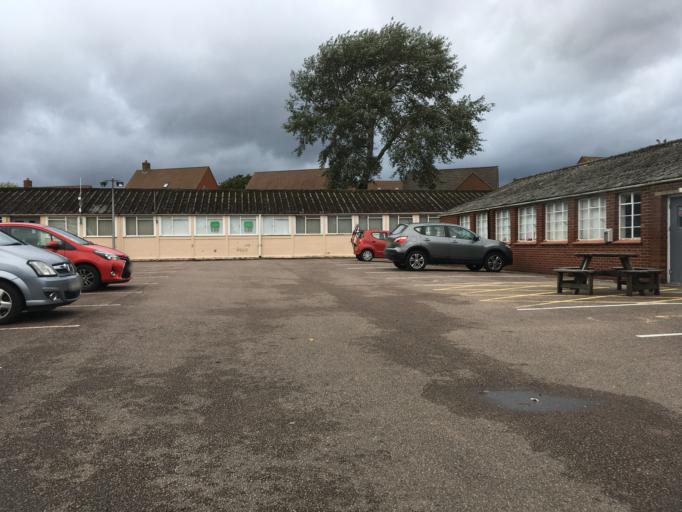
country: GB
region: England
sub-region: Buckinghamshire
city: Bletchley
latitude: 51.9984
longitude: -0.7432
